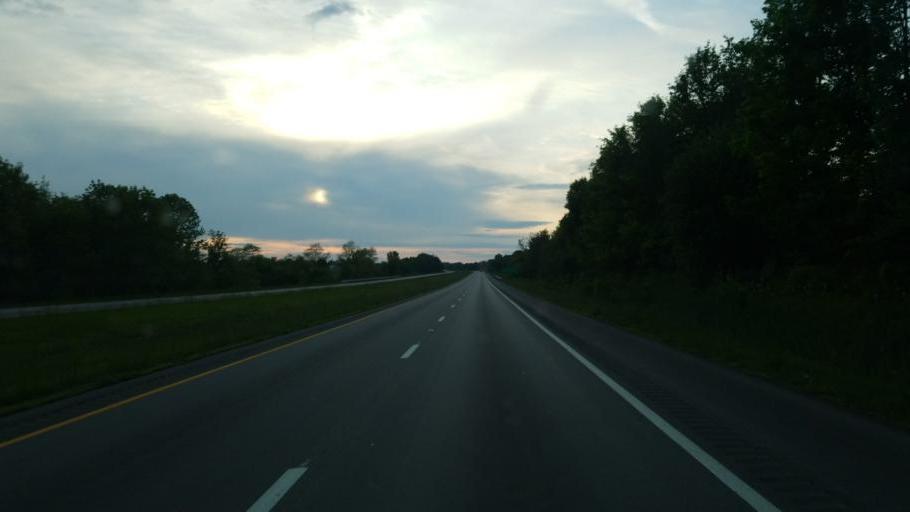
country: US
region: Ohio
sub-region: Stark County
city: Brewster
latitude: 40.7829
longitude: -81.6102
